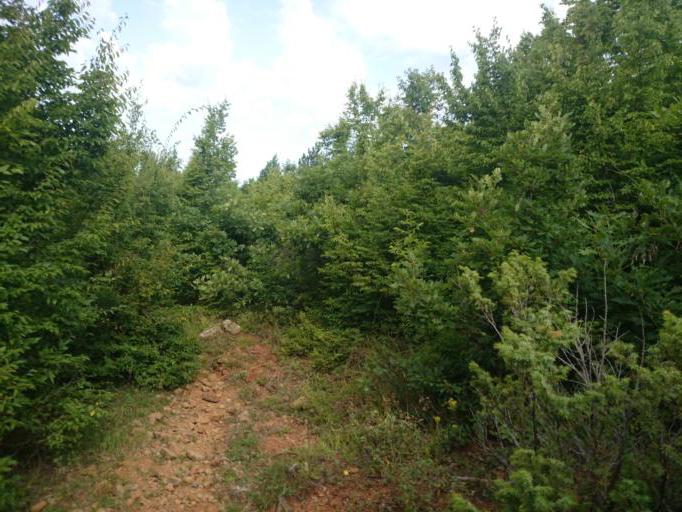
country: AL
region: Elbasan
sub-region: Rrethi i Gramshit
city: Lenias
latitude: 40.7707
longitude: 20.3367
